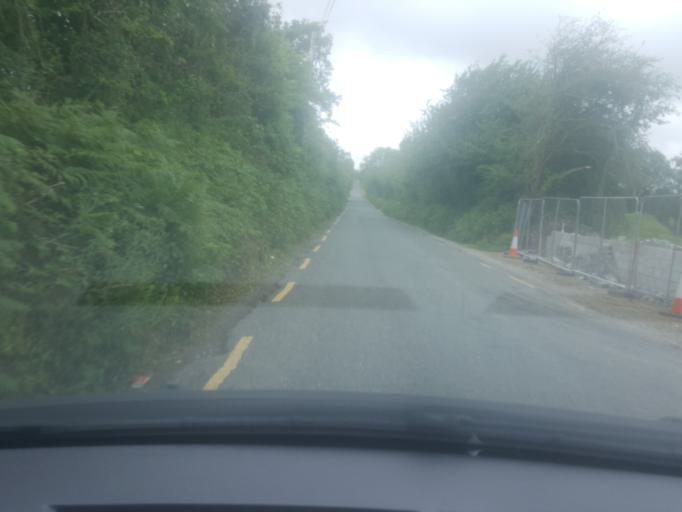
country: IE
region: Munster
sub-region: Ciarrai
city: Cill Airne
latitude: 52.0839
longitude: -9.5069
